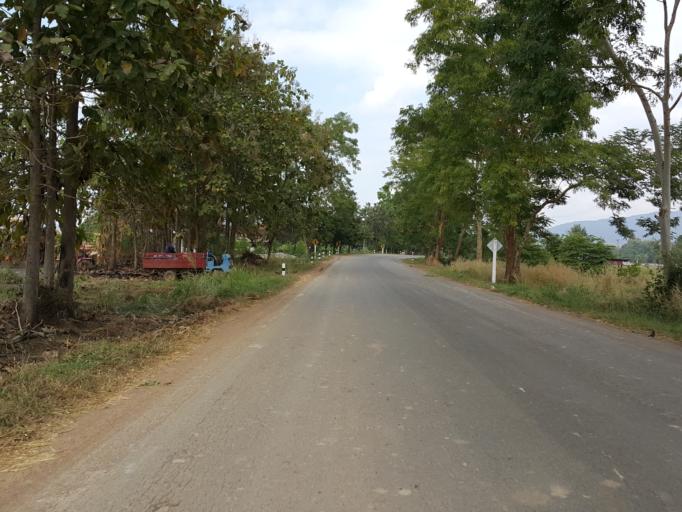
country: TH
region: Sukhothai
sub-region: Amphoe Si Satchanalai
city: Si Satchanalai
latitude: 17.4698
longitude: 99.6405
